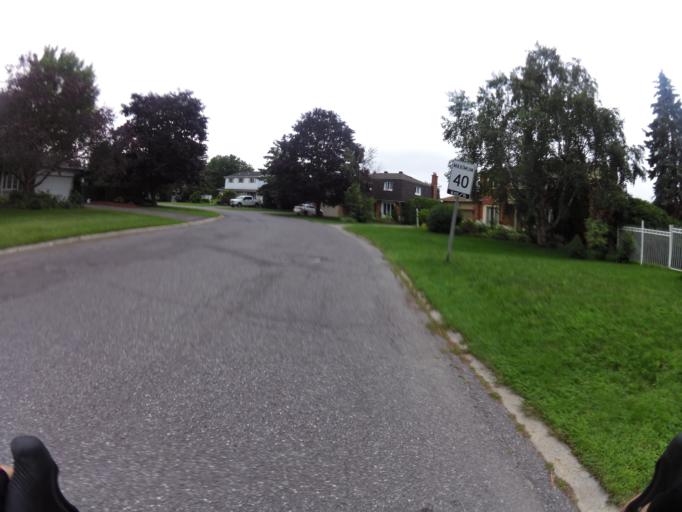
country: CA
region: Ontario
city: Ottawa
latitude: 45.3225
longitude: -75.7076
